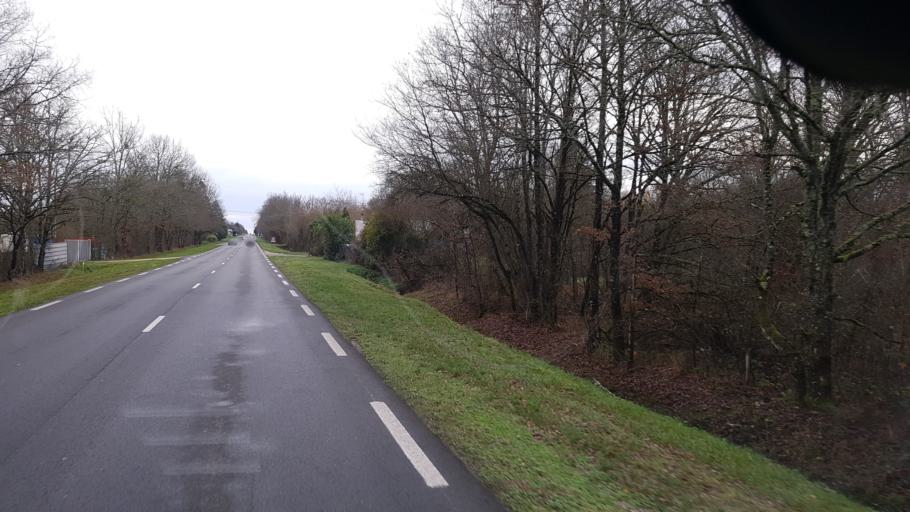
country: FR
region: Centre
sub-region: Departement du Loiret
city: Menestreau-en-Villette
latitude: 47.6571
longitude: 1.9837
